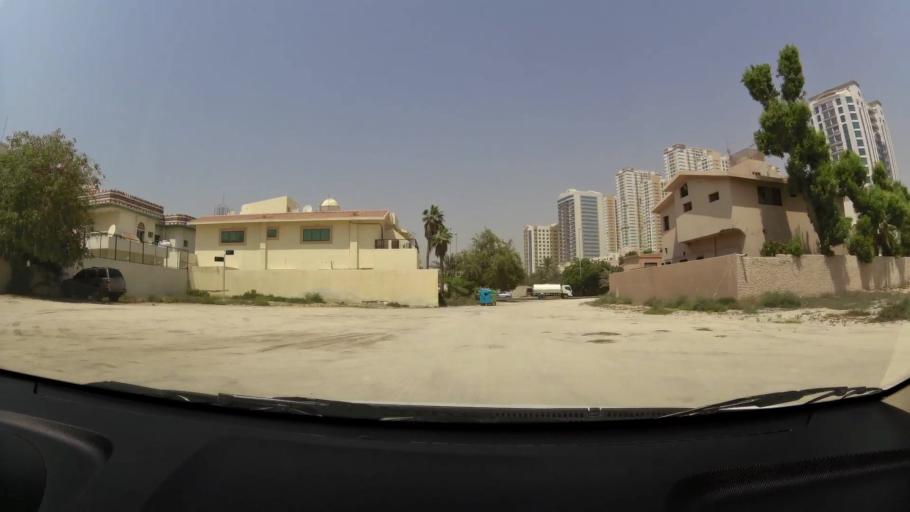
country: AE
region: Ajman
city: Ajman
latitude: 25.3950
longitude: 55.4253
